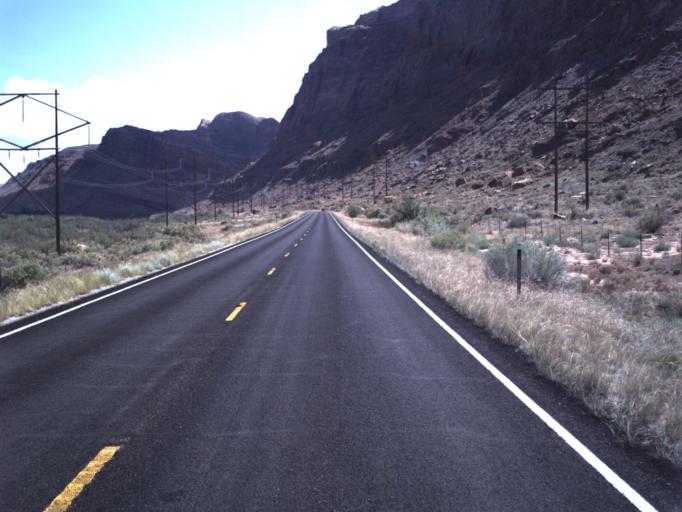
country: US
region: Utah
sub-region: Grand County
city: Moab
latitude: 38.5902
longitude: -109.5942
